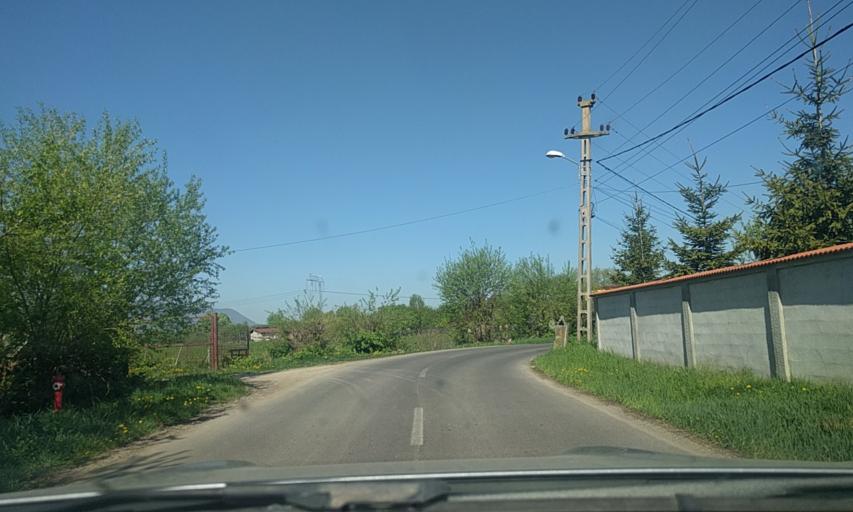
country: RO
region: Brasov
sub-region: Comuna Bod
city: Colonia Bod
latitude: 45.7102
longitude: 25.5691
